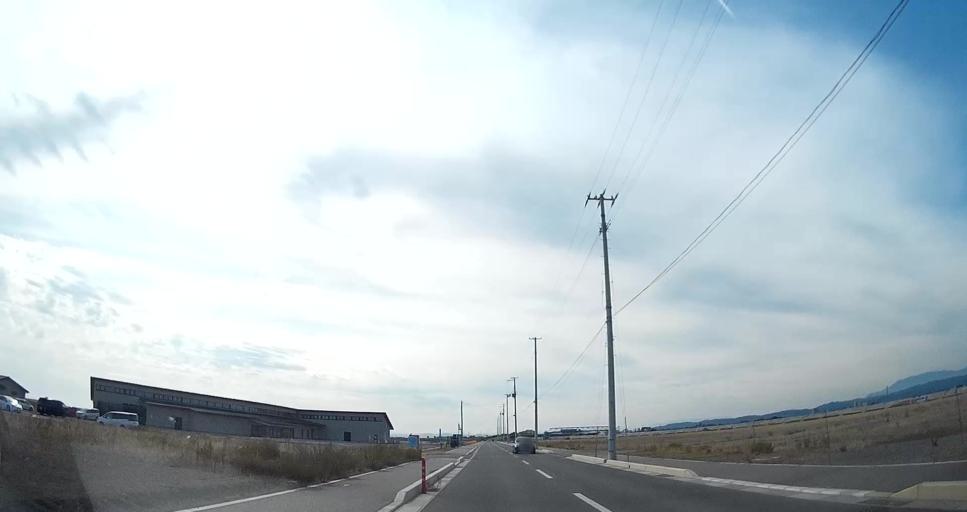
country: JP
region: Miyagi
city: Iwanuma
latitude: 38.1692
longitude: 140.9517
